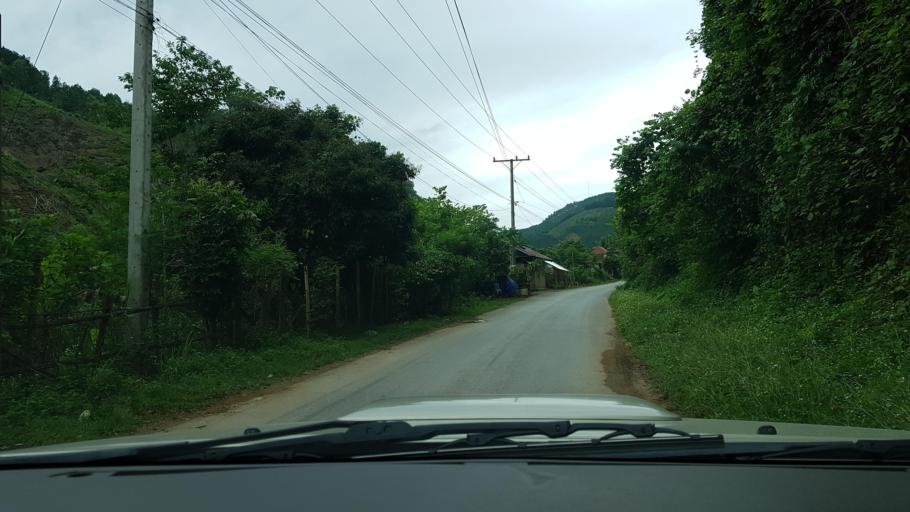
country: LA
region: Phongsali
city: Khoa
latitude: 21.0726
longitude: 102.5014
